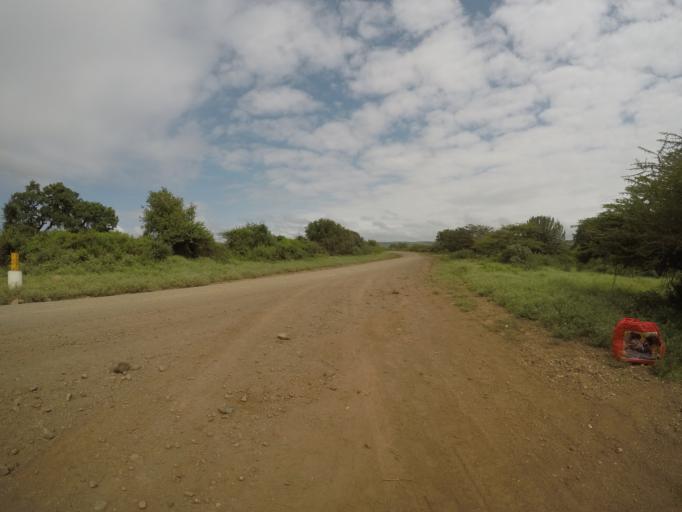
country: ZA
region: KwaZulu-Natal
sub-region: uThungulu District Municipality
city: Empangeni
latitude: -28.6218
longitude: 31.8664
